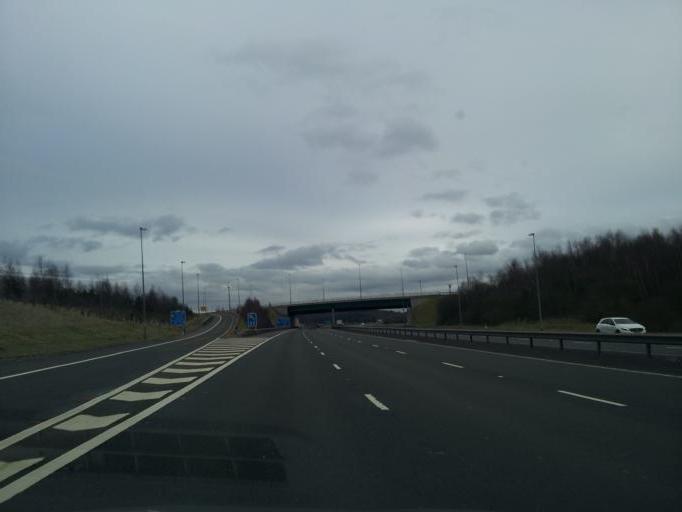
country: GB
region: England
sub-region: Staffordshire
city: Shenstone
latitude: 52.6409
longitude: -1.8154
